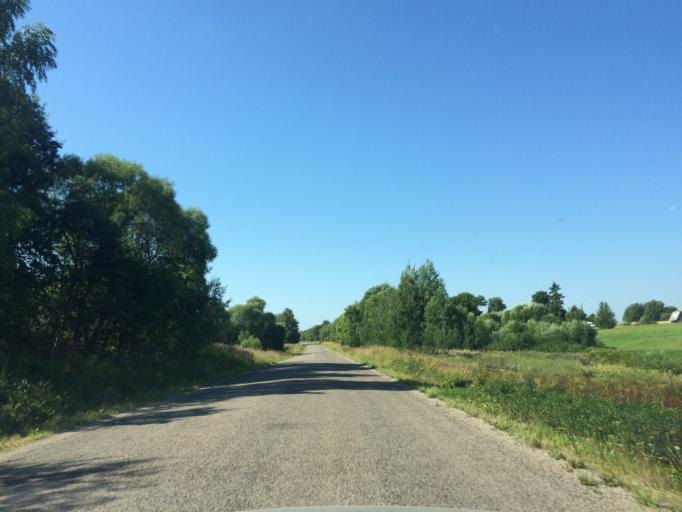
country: LV
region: Rezekne
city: Rezekne
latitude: 56.4998
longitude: 27.2924
